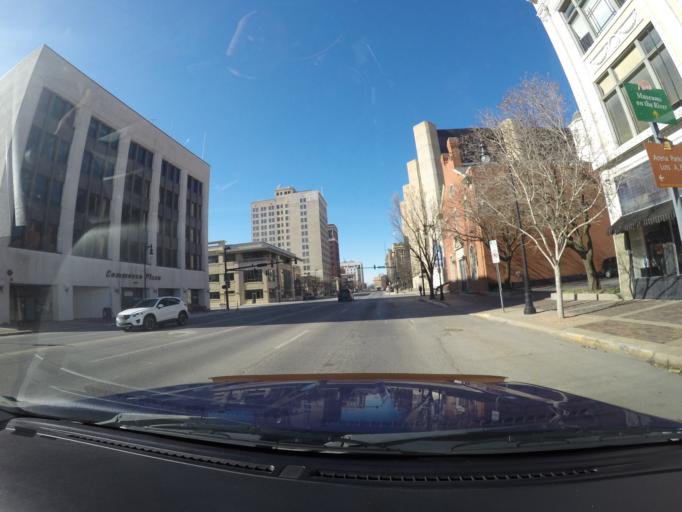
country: US
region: Kansas
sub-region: Sedgwick County
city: Wichita
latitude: 37.6861
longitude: -97.3337
